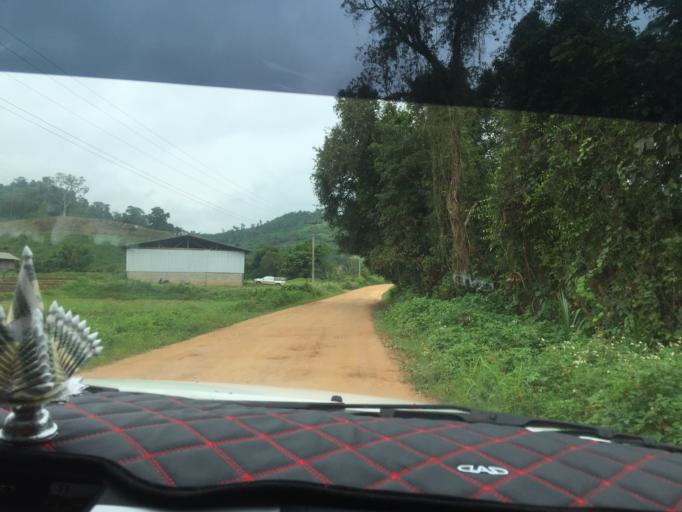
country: TH
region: Phayao
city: Phu Sang
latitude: 19.6780
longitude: 100.5068
